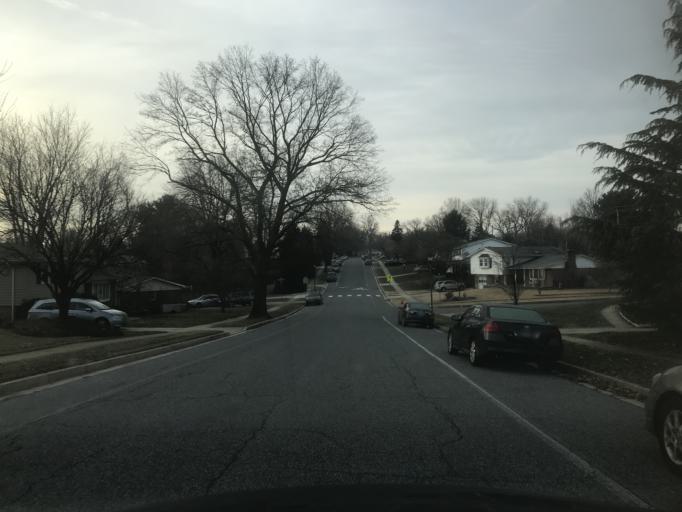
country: US
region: Maryland
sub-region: Baltimore County
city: Timonium
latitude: 39.4547
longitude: -76.6161
